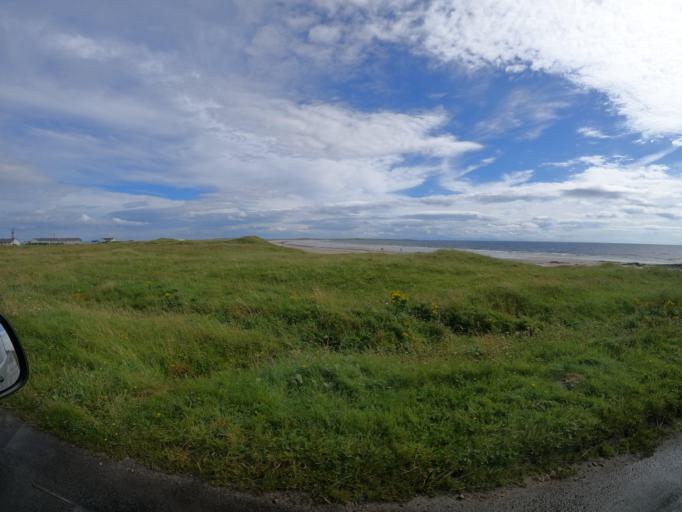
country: GB
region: Scotland
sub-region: Eilean Siar
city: Barra
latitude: 56.4882
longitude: -6.8794
